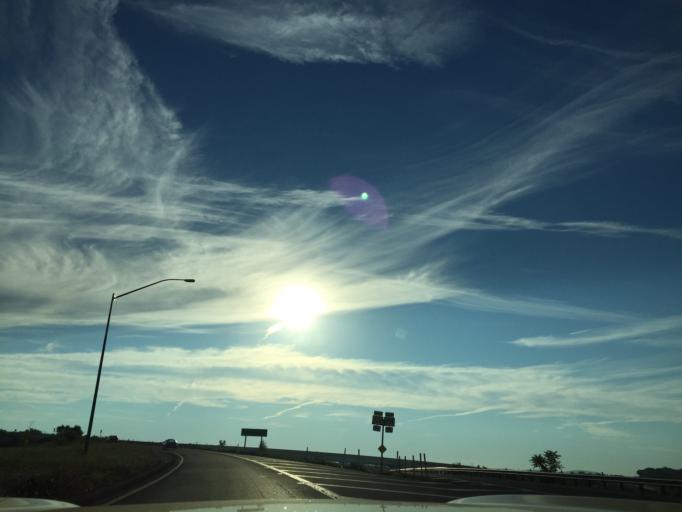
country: US
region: Pennsylvania
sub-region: Lehigh County
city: Breinigsville
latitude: 40.5396
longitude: -75.6249
